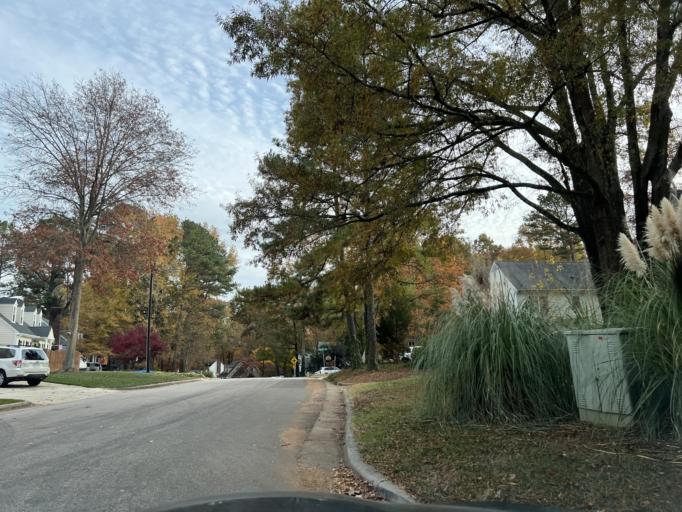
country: US
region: North Carolina
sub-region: Wake County
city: Wake Forest
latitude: 35.8974
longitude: -78.5941
